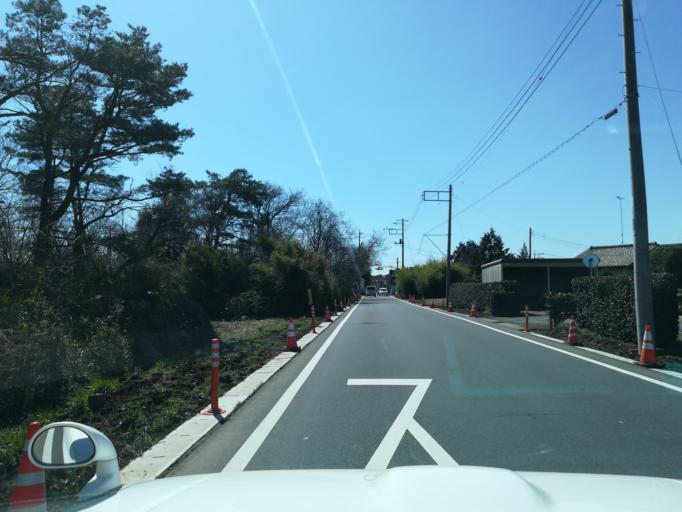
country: JP
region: Ibaraki
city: Ushiku
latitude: 35.9875
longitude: 140.1791
